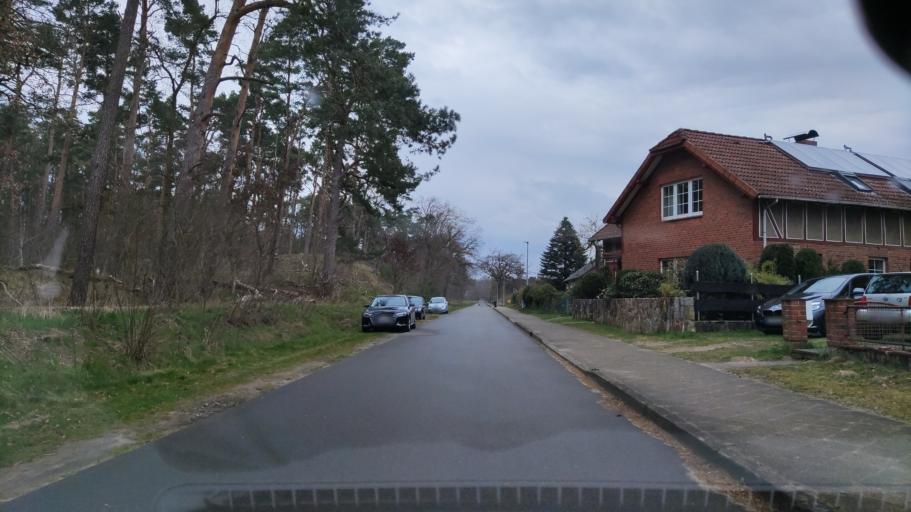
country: DE
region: Lower Saxony
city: Tosterglope
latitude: 53.2728
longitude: 10.8005
